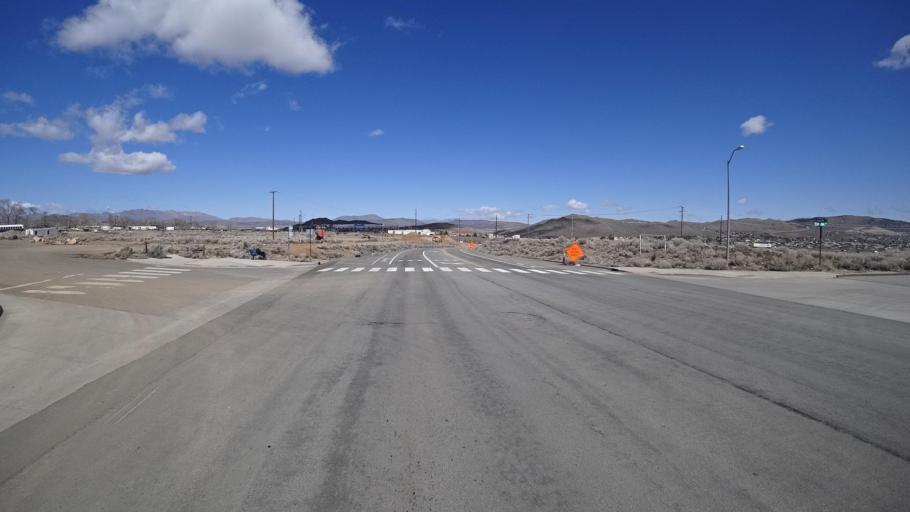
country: US
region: Nevada
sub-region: Washoe County
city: Golden Valley
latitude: 39.6078
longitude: -119.8530
